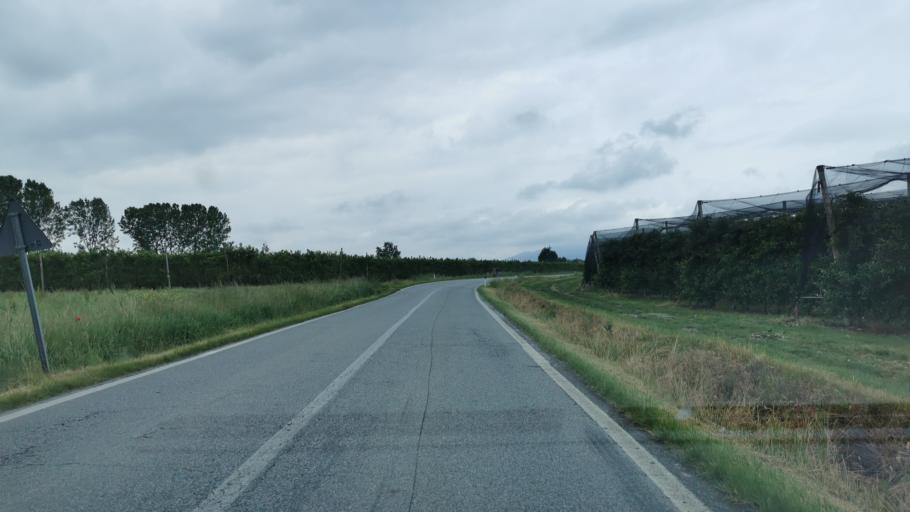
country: IT
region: Piedmont
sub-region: Provincia di Cuneo
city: Lagnasco
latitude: 44.5975
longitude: 7.5670
